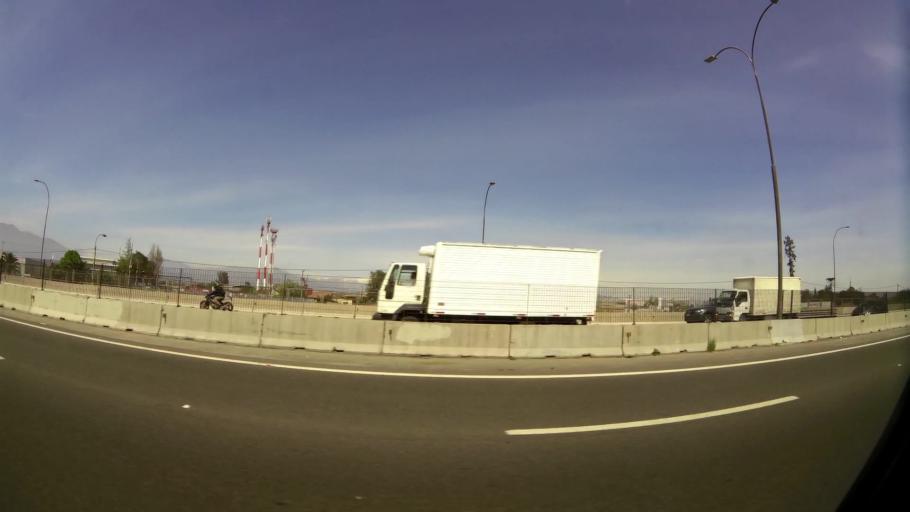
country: CL
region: Santiago Metropolitan
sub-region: Provincia de Maipo
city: San Bernardo
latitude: -33.5422
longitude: -70.6880
